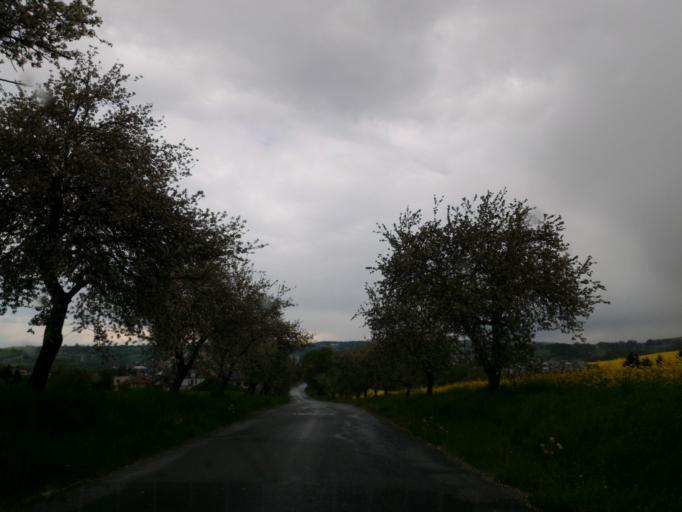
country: CZ
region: Vysocina
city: Ledec nad Sazavou
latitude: 49.6838
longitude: 15.2850
